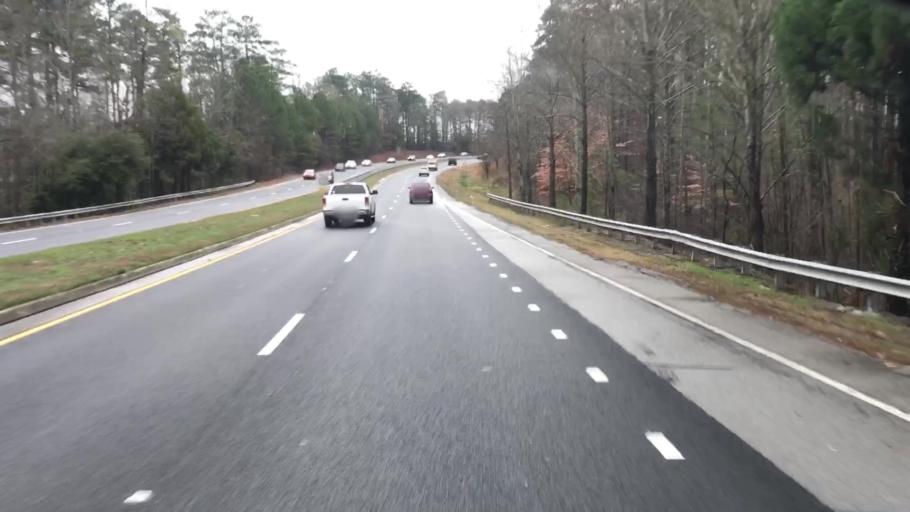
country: US
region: Georgia
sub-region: Gwinnett County
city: Snellville
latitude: 33.8908
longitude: -84.0491
